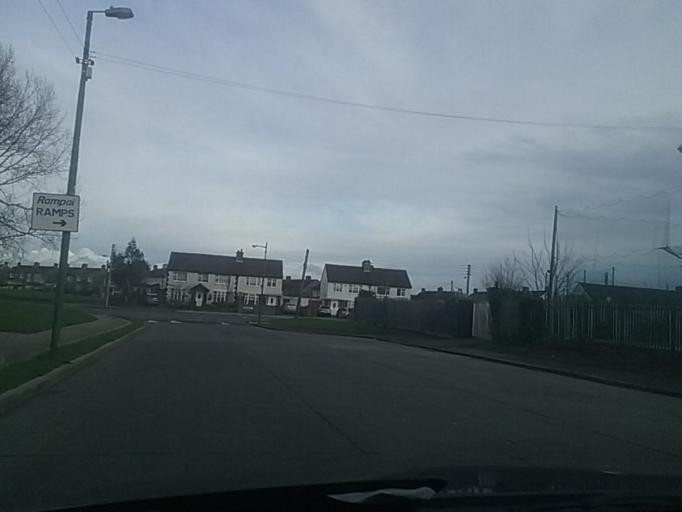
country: IE
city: Coolock
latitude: 53.3825
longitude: -6.1954
